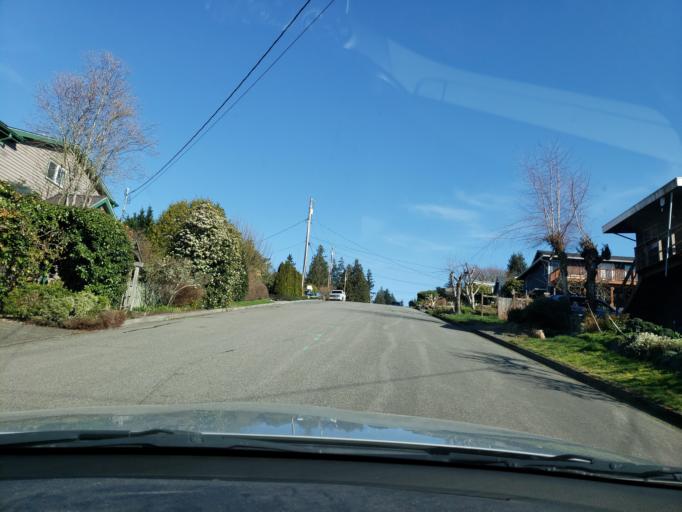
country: US
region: Washington
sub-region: Snohomish County
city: Edmonds
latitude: 47.8049
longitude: -122.3721
